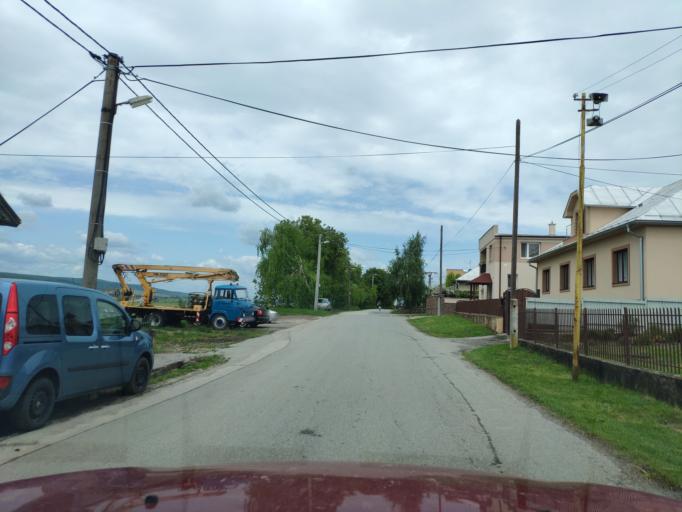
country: SK
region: Kosicky
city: Kosice
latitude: 48.7143
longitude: 21.3487
